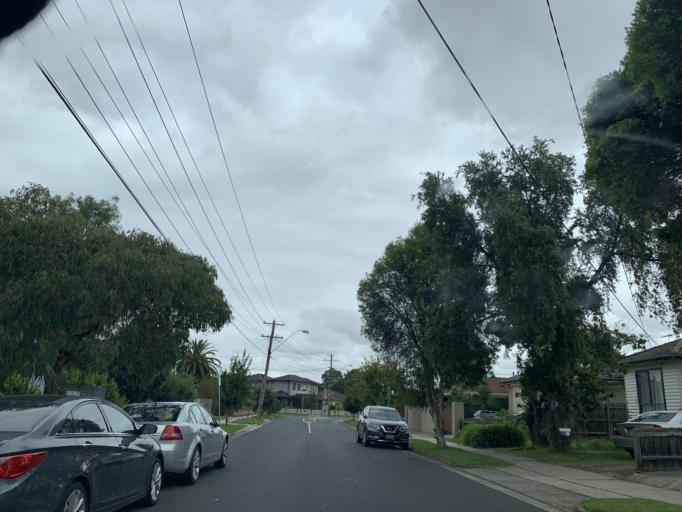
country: AU
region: Victoria
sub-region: Moreland
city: Oak Park
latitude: -37.7210
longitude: 144.9162
